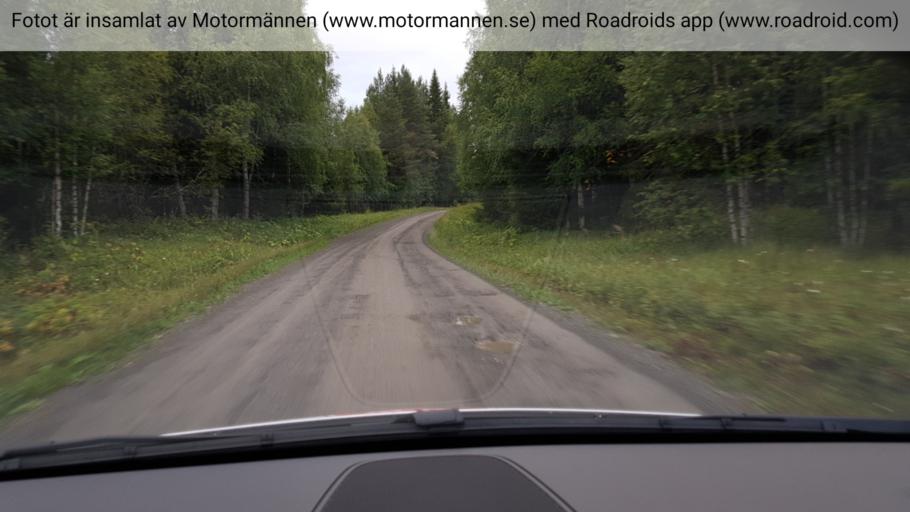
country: SE
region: Jaemtland
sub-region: OEstersunds Kommun
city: Lit
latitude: 63.4834
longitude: 14.7555
